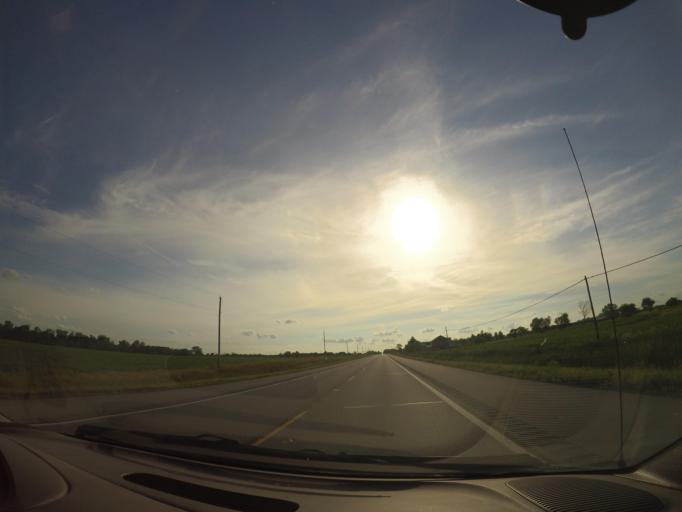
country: US
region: Ohio
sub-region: Williams County
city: Bryan
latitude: 41.4414
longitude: -84.6067
